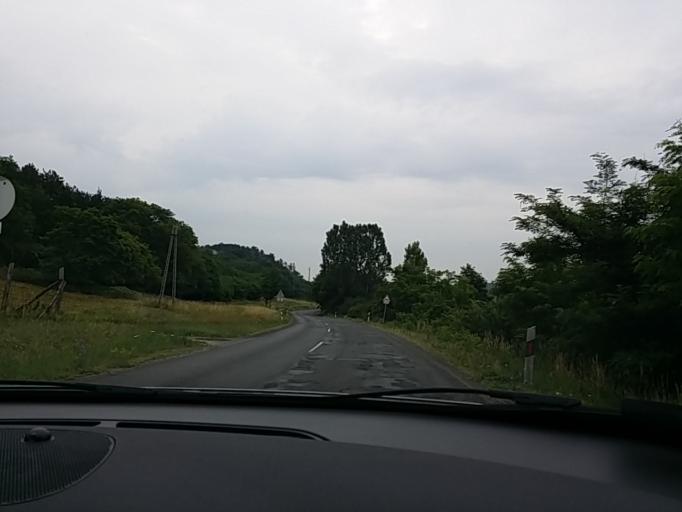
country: HU
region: Nograd
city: Batonyterenye
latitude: 47.9974
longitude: 19.8561
